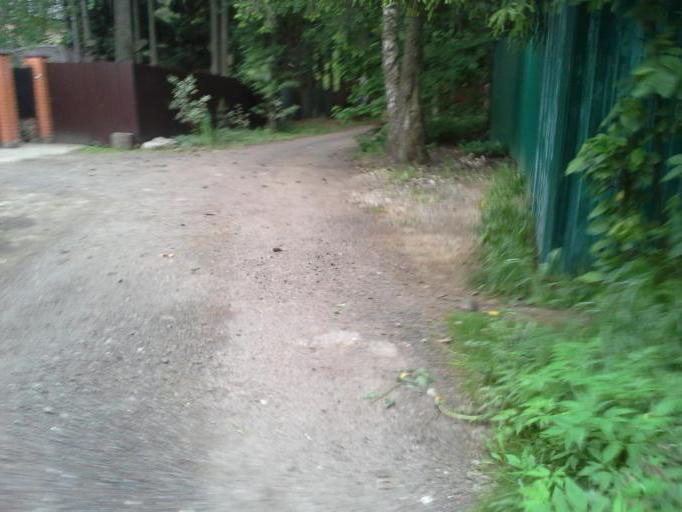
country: RU
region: Moskovskaya
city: Lesnoy Gorodok
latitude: 55.6434
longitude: 37.1887
